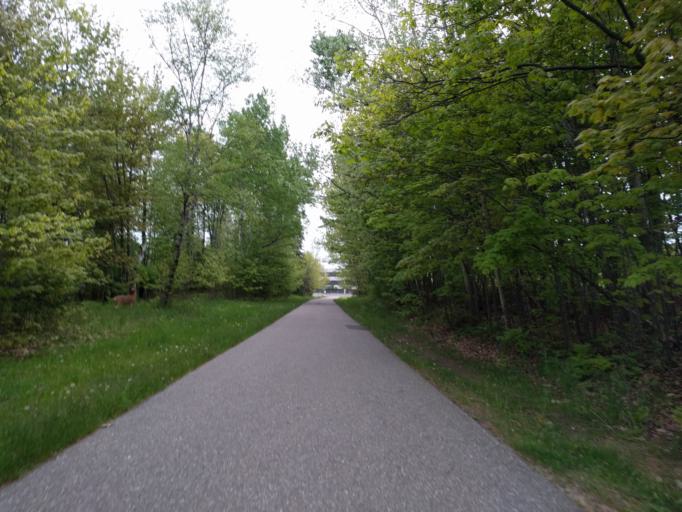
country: US
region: Michigan
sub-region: Marquette County
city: Trowbridge Park
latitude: 46.5551
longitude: -87.4174
